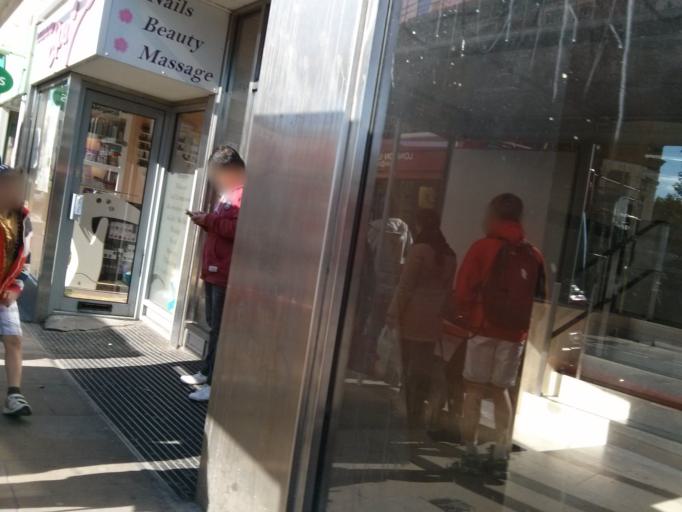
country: GB
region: England
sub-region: Greater London
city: Richmond
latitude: 51.4629
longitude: -0.3024
